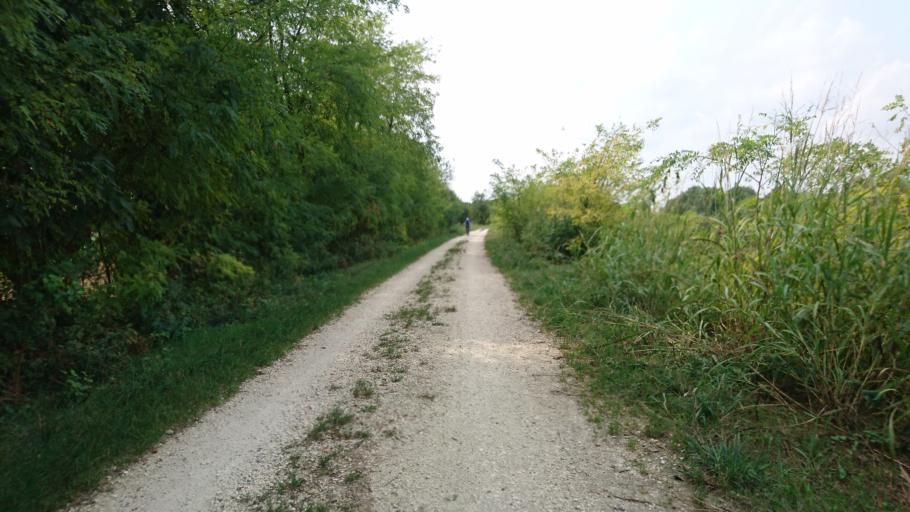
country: IT
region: Veneto
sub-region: Provincia di Padova
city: Saletto
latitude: 45.4706
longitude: 11.8570
